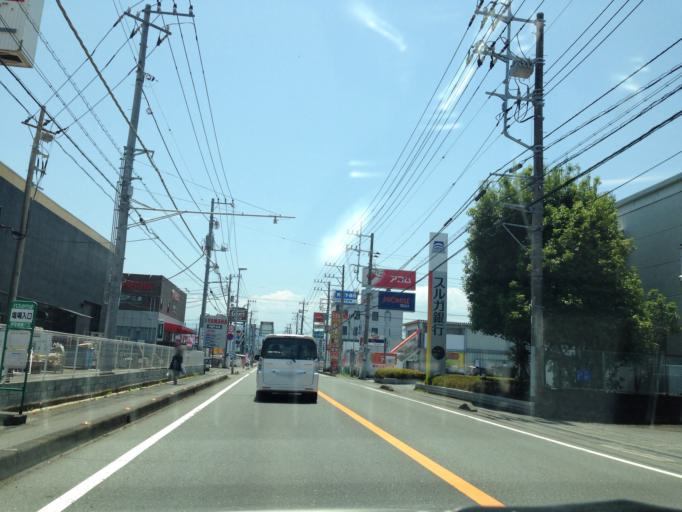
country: JP
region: Shizuoka
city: Numazu
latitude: 35.0801
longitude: 138.8707
